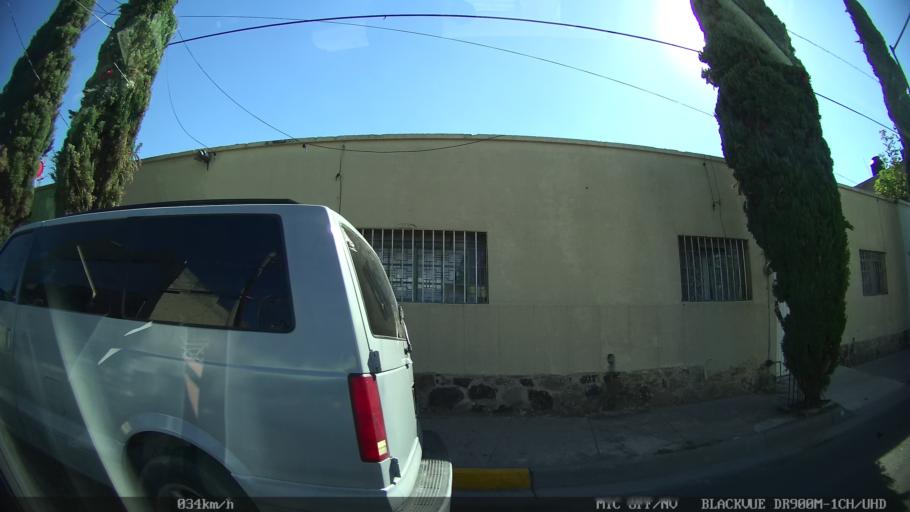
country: MX
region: Jalisco
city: Tlaquepaque
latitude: 20.6715
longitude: -103.2805
